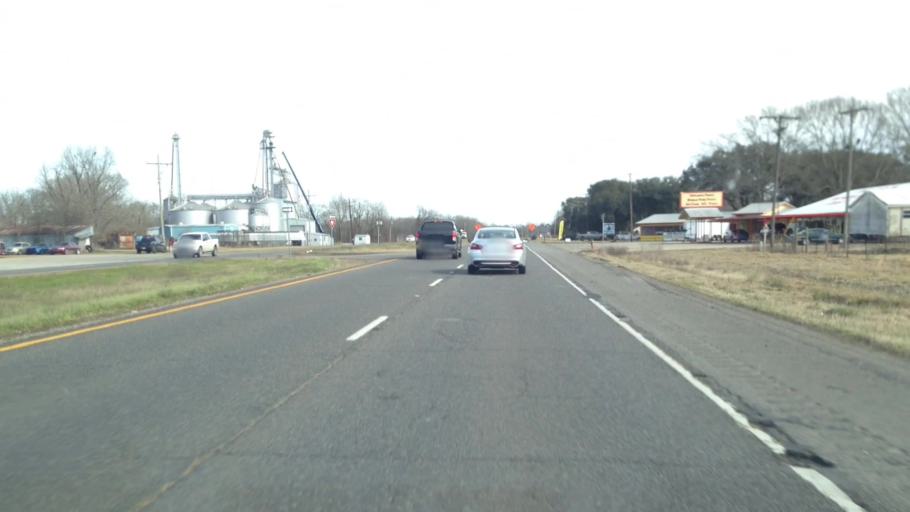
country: US
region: Louisiana
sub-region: Saint Landry Parish
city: Port Barre
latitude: 30.5477
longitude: -91.9903
